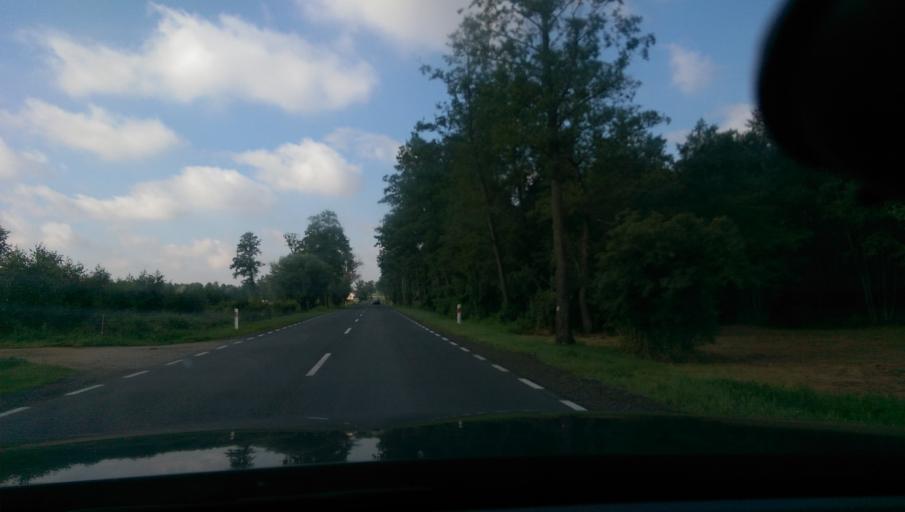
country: PL
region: Masovian Voivodeship
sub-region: Powiat plonski
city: Sochocin
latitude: 52.7100
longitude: 20.4950
